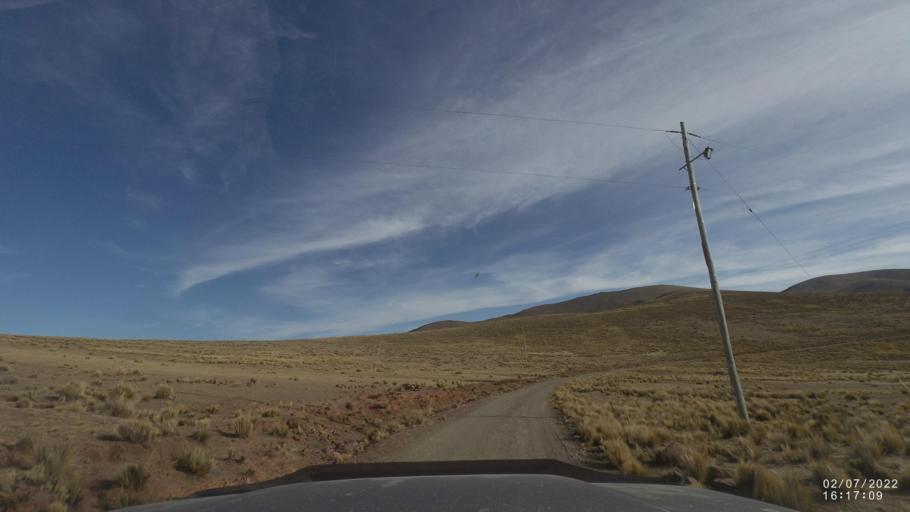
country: BO
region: Cochabamba
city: Irpa Irpa
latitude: -17.9245
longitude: -66.4355
